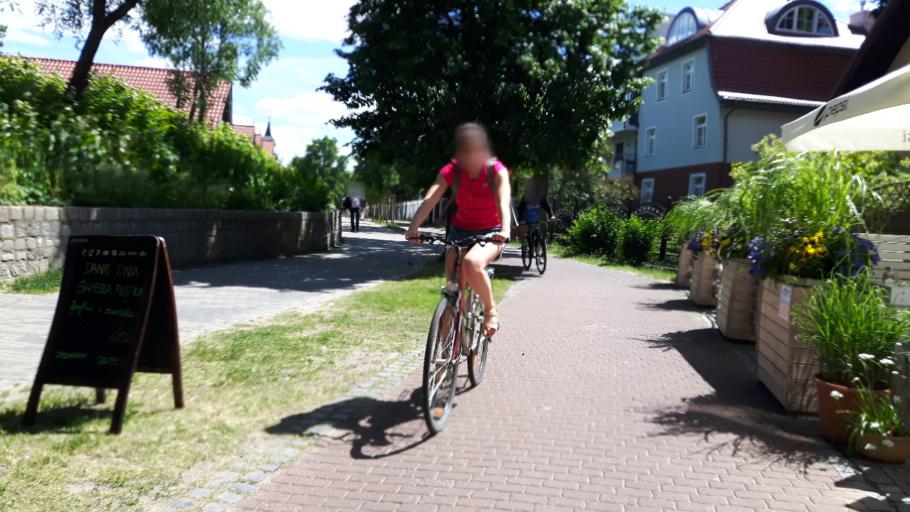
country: PL
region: Pomeranian Voivodeship
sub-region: Sopot
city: Sopot
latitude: 54.4379
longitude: 18.5789
